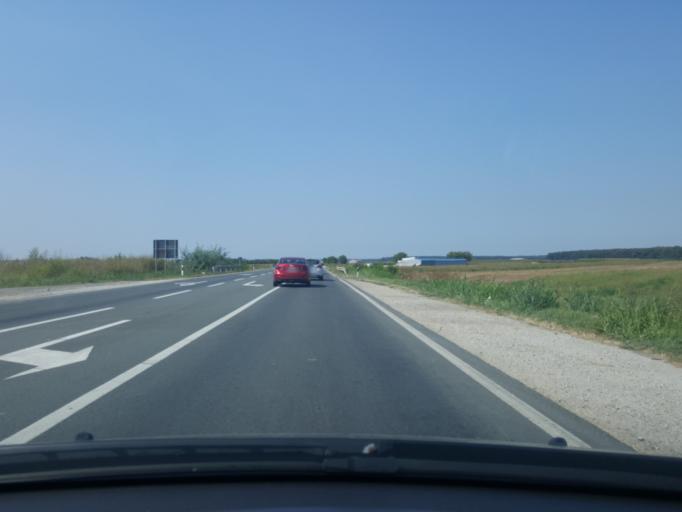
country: RS
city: Klenak
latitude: 44.7743
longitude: 19.7254
